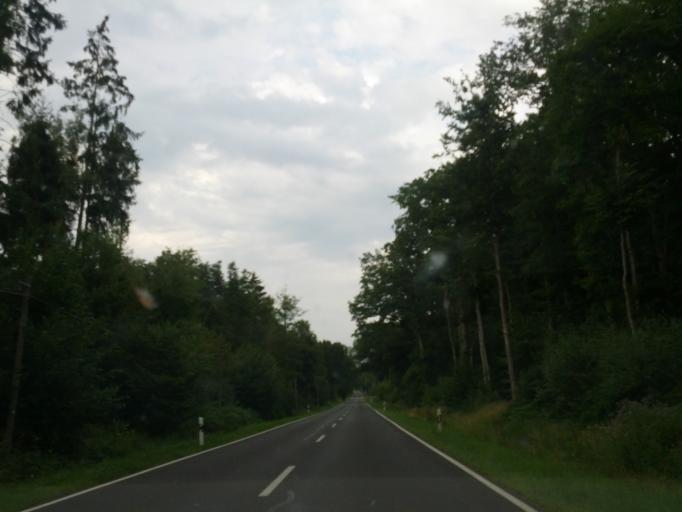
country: DE
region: Mecklenburg-Vorpommern
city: Kropelin
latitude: 54.0462
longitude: 11.7968
